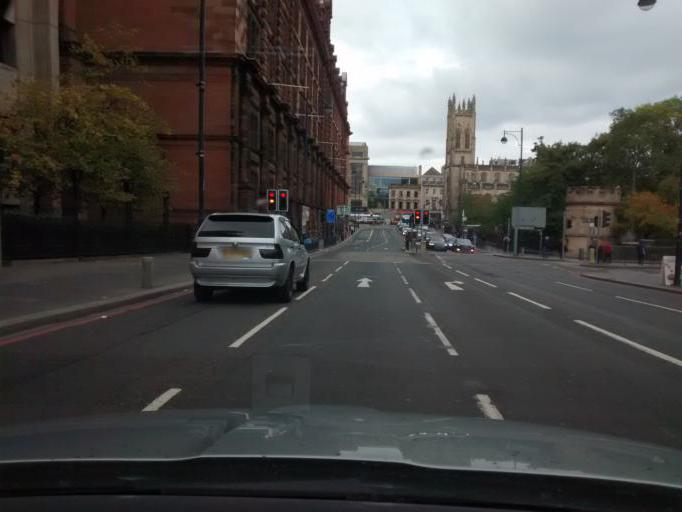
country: GB
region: Scotland
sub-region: Edinburgh
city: Edinburgh
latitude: 55.9484
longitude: -3.2065
